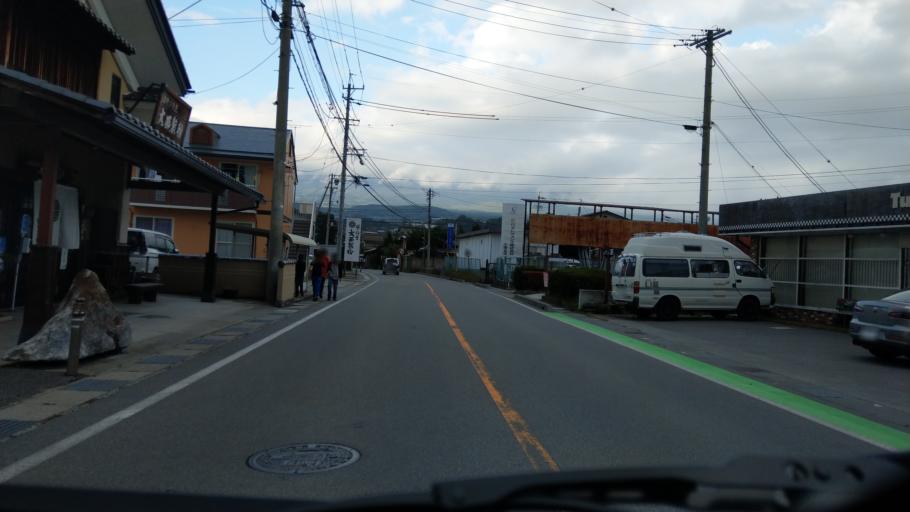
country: JP
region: Nagano
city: Komoro
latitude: 36.3140
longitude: 138.4311
